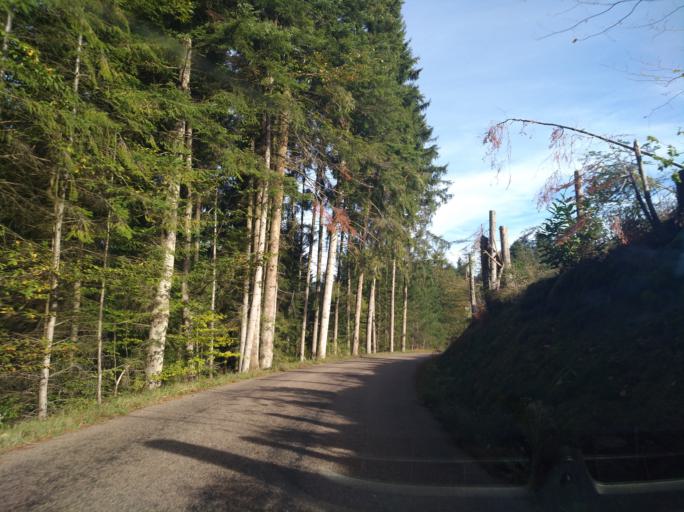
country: FR
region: Bourgogne
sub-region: Departement de Saone-et-Loire
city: Chauffailles
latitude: 46.2011
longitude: 4.4024
